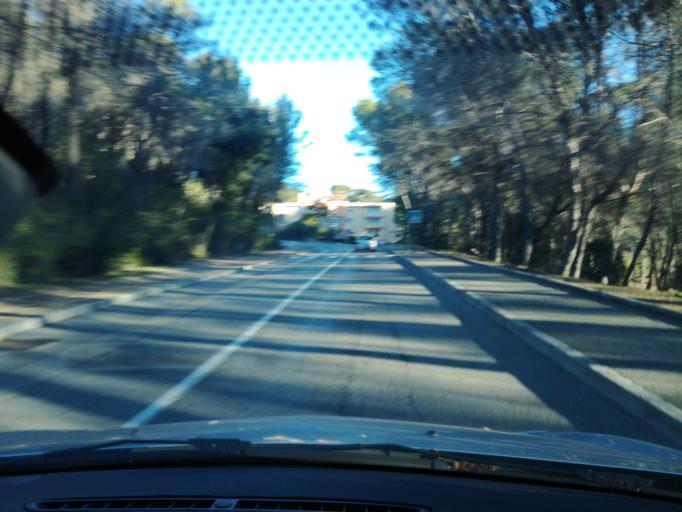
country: FR
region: Provence-Alpes-Cote d'Azur
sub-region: Departement des Alpes-Maritimes
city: Vallauris
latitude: 43.6131
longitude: 7.0537
